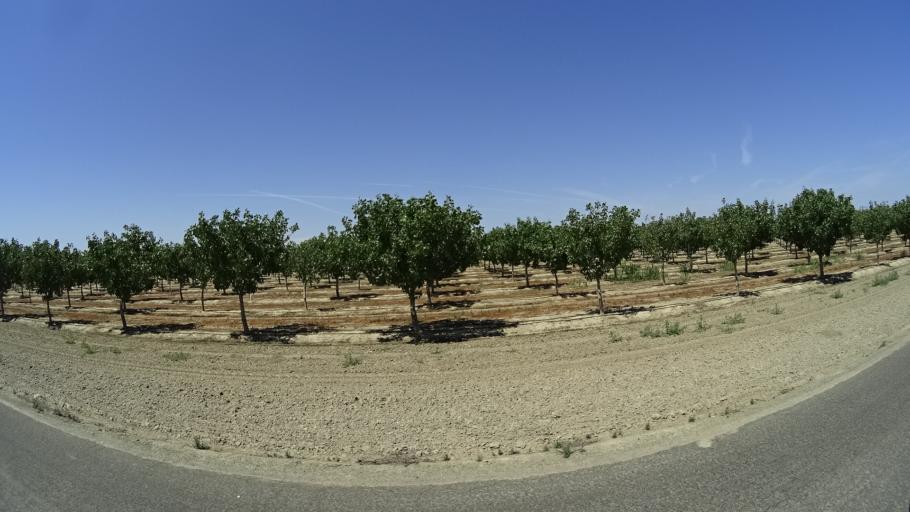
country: US
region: California
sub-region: Kings County
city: Armona
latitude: 36.2512
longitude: -119.7268
